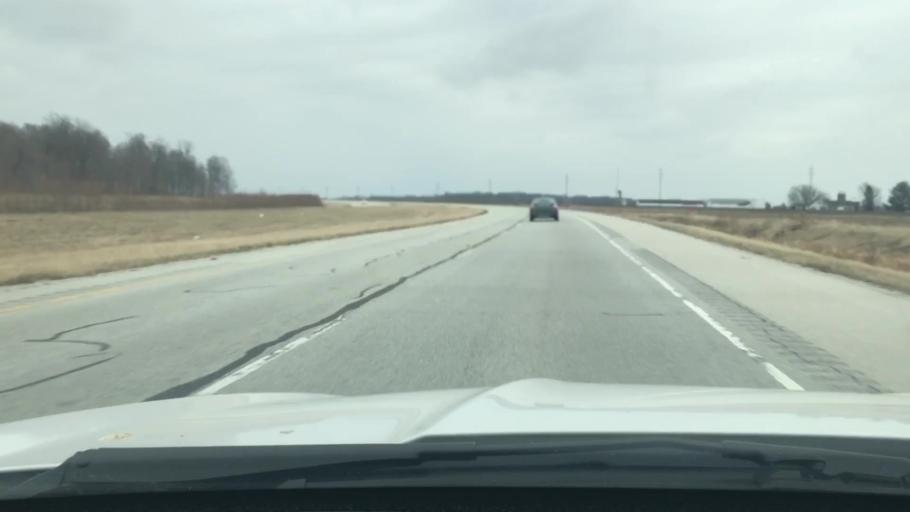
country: US
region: Indiana
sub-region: Cass County
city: Georgetown
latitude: 40.6824
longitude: -86.5015
